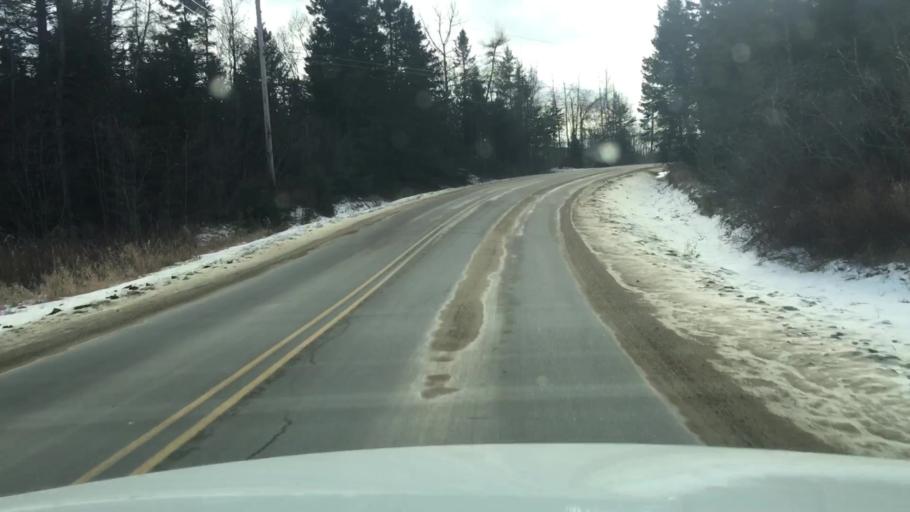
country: US
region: Maine
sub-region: Washington County
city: Jonesport
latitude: 44.6282
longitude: -67.5968
